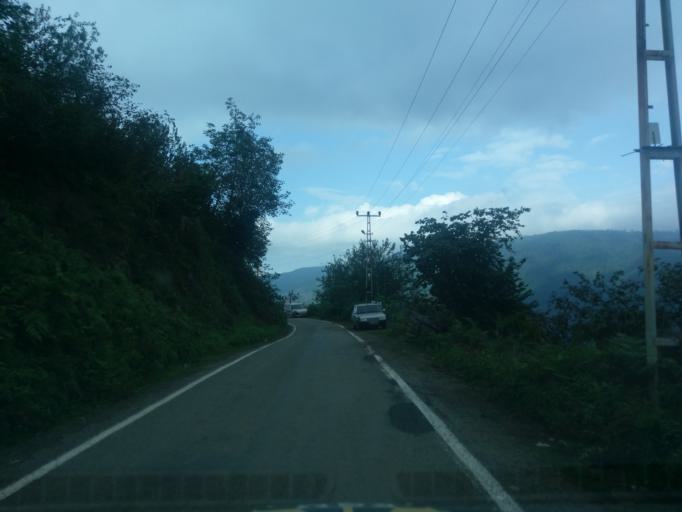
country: TR
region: Ordu
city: Camas
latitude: 40.9032
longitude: 37.6119
